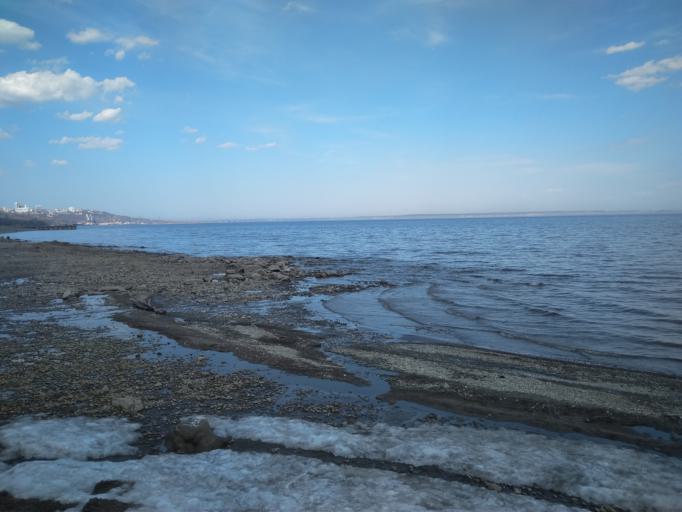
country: RU
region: Ulyanovsk
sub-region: Ulyanovskiy Rayon
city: Ulyanovsk
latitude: 54.2694
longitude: 48.3586
